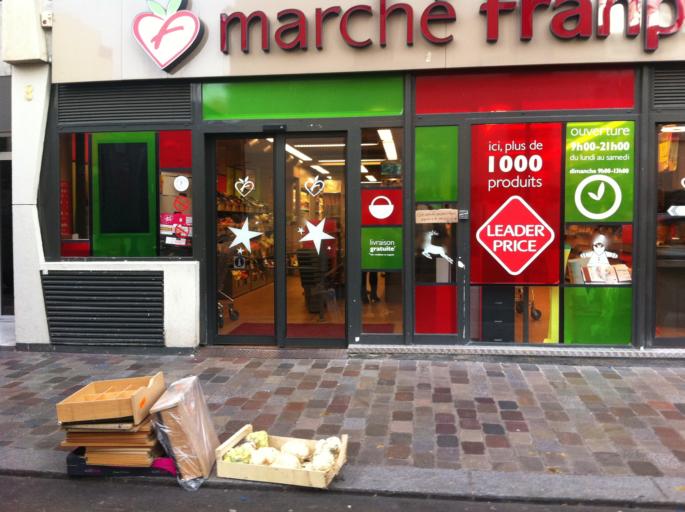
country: FR
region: Ile-de-France
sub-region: Paris
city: Paris
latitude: 48.8480
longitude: 2.3773
